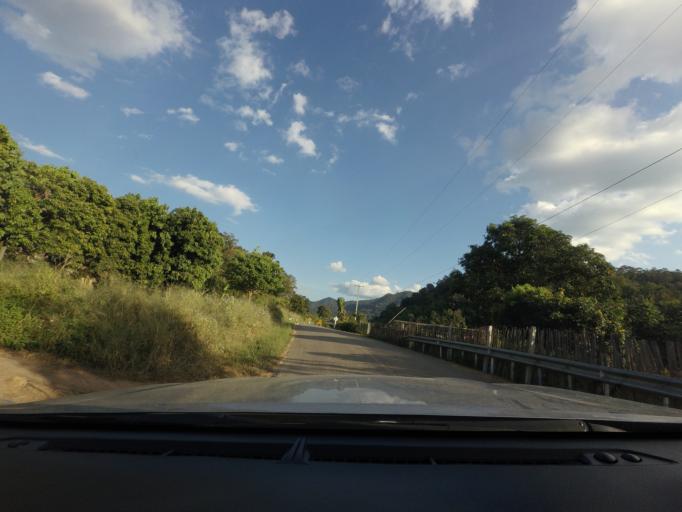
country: TH
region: Chiang Mai
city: Phrao
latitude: 19.5145
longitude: 99.1669
